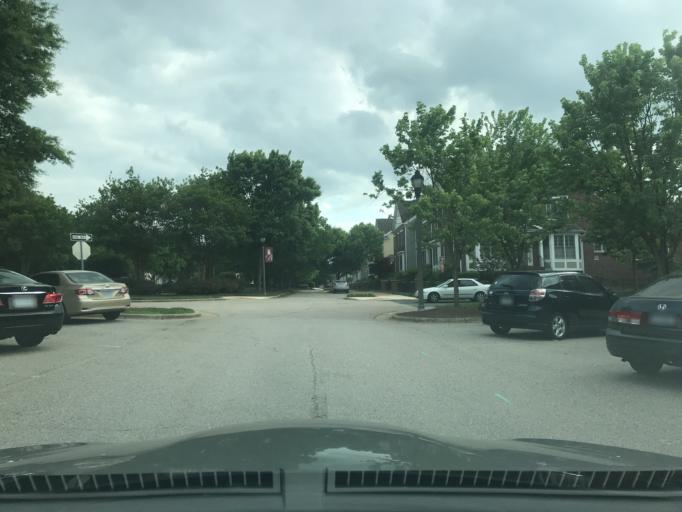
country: US
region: North Carolina
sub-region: Wake County
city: Wake Forest
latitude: 35.9291
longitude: -78.5646
